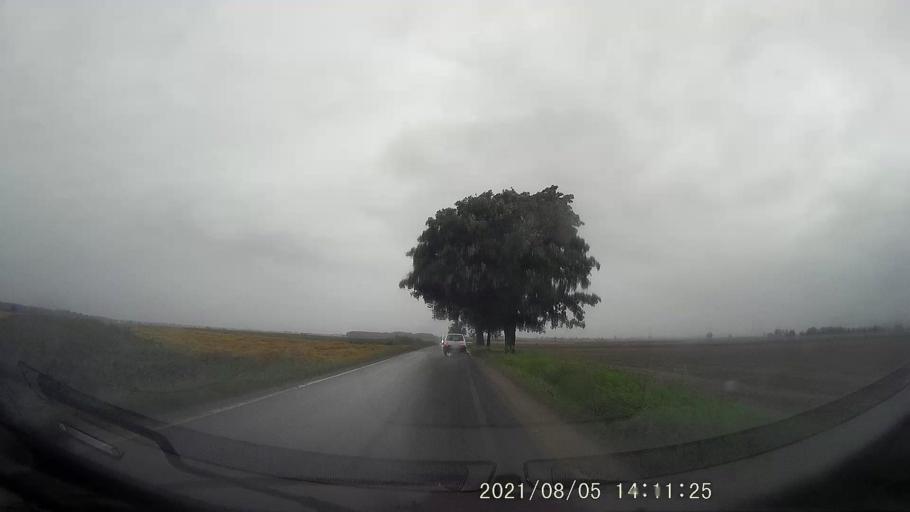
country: PL
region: Opole Voivodeship
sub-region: Powiat krapkowicki
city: Strzeleczki
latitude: 50.4722
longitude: 17.7775
